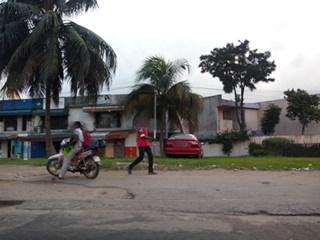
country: CI
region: Lagunes
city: Abobo
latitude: 5.3675
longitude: -3.9984
